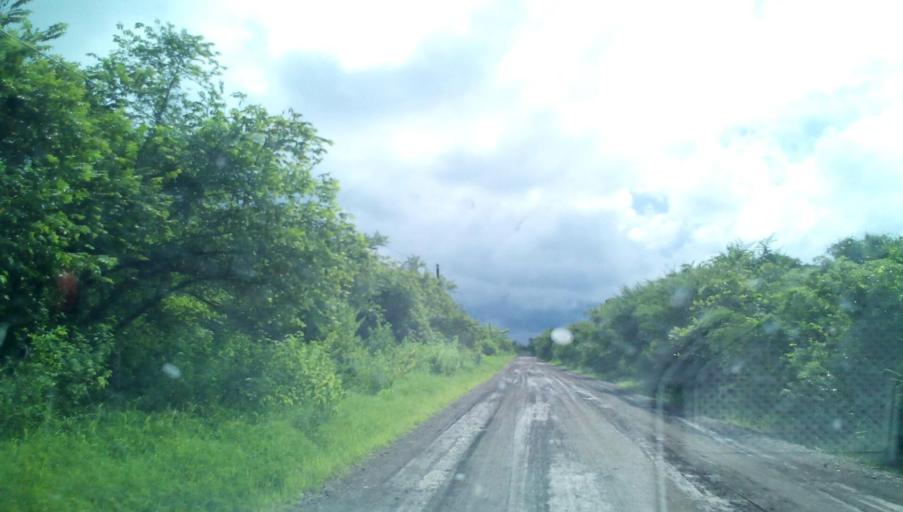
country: MX
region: Veracruz
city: Panuco
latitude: 21.8507
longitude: -98.1608
